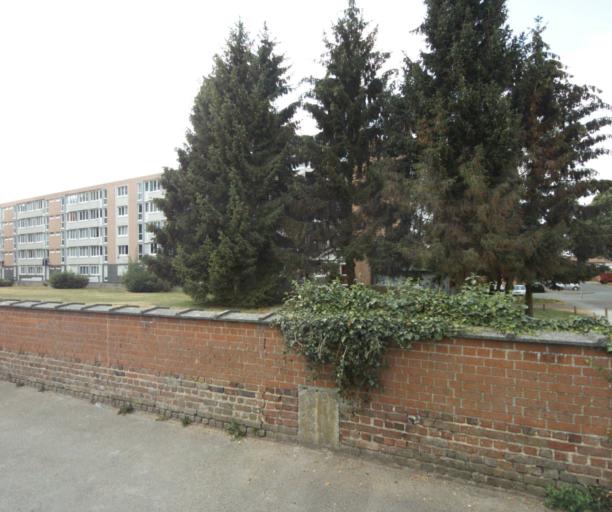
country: FR
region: Nord-Pas-de-Calais
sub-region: Departement du Nord
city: Marquette-lez-Lille
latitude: 50.6685
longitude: 3.0697
